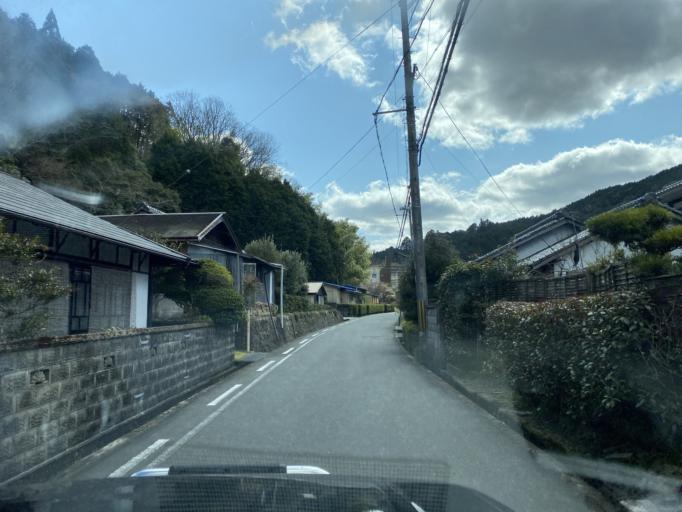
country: JP
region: Nara
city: Nara-shi
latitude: 34.7330
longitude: 135.9524
